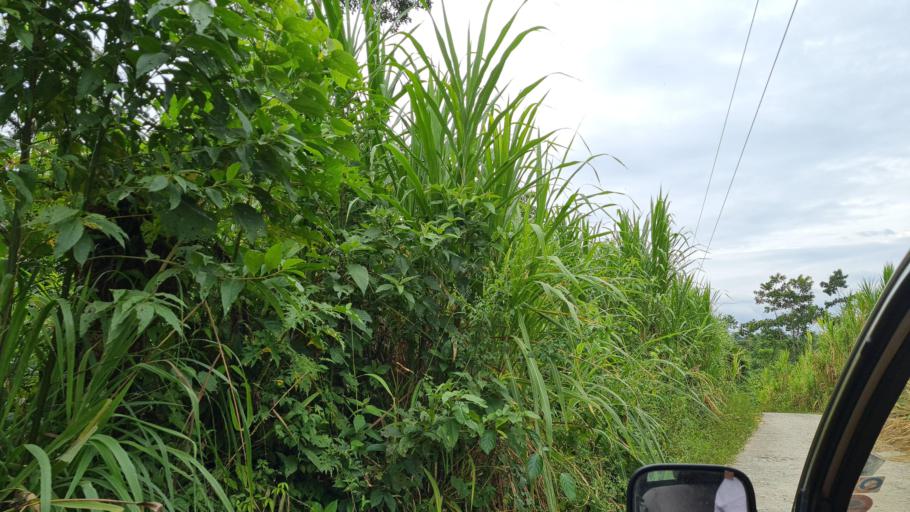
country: EC
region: Napo
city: Tena
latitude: -1.0009
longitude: -77.7613
